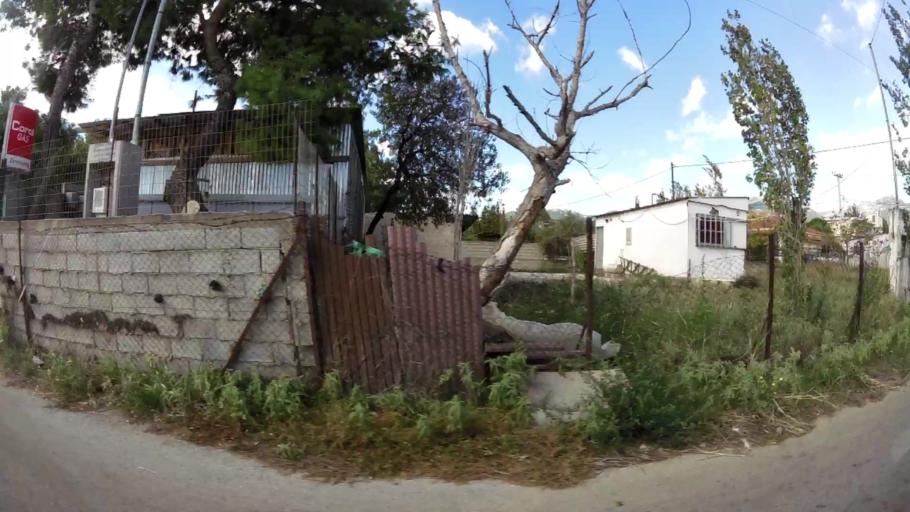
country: GR
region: Attica
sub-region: Nomarchia Anatolikis Attikis
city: Thrakomakedones
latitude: 38.1082
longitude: 23.7607
